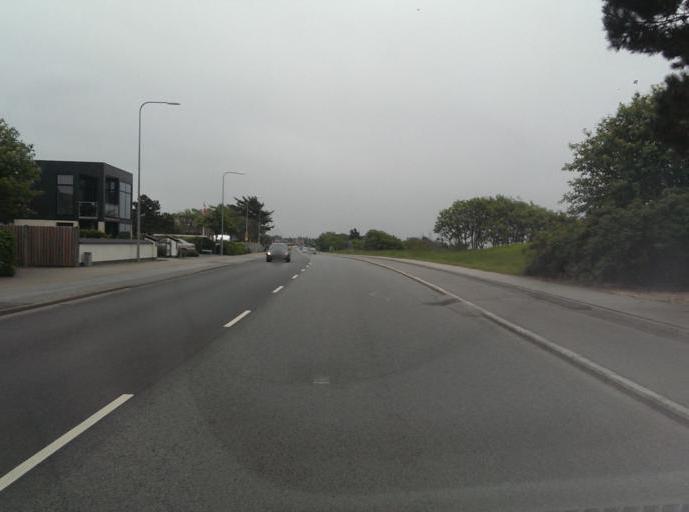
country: DK
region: South Denmark
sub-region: Fano Kommune
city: Nordby
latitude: 55.5013
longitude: 8.3897
